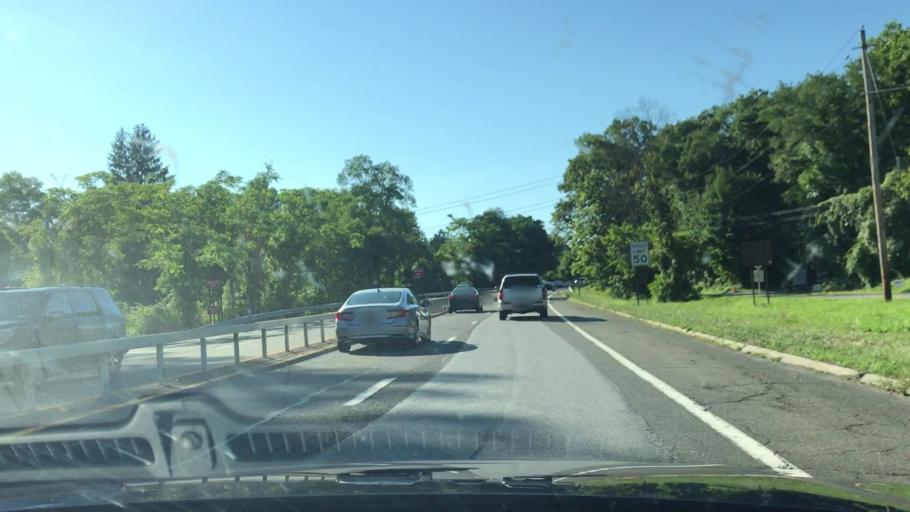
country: US
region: New York
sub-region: Westchester County
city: Valhalla
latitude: 41.0870
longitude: -73.7884
